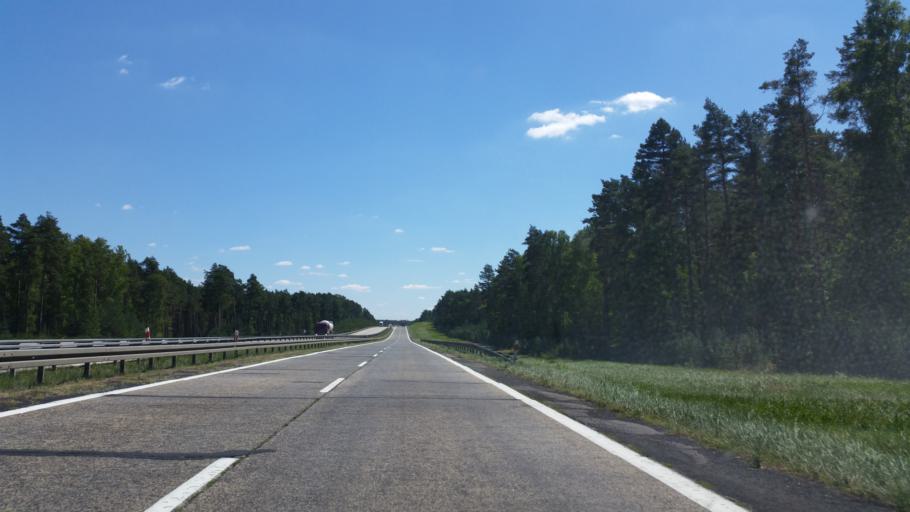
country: PL
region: Lubusz
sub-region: Powiat zaganski
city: Malomice
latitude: 51.4093
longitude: 15.5016
